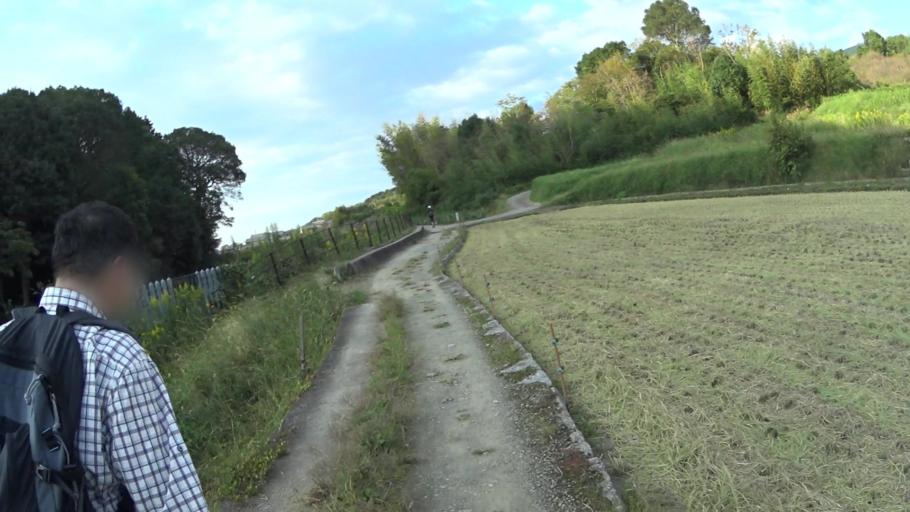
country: JP
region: Nara
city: Tenri
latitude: 34.5508
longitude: 135.8508
